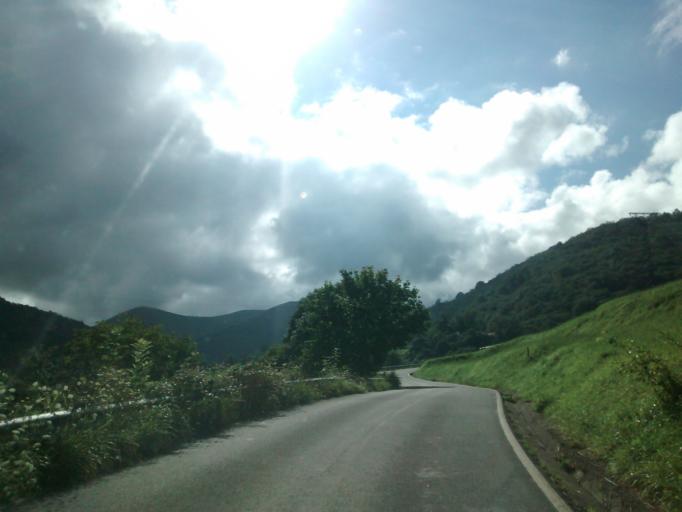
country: ES
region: Cantabria
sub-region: Provincia de Cantabria
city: Ruente
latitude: 43.1917
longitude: -4.2686
